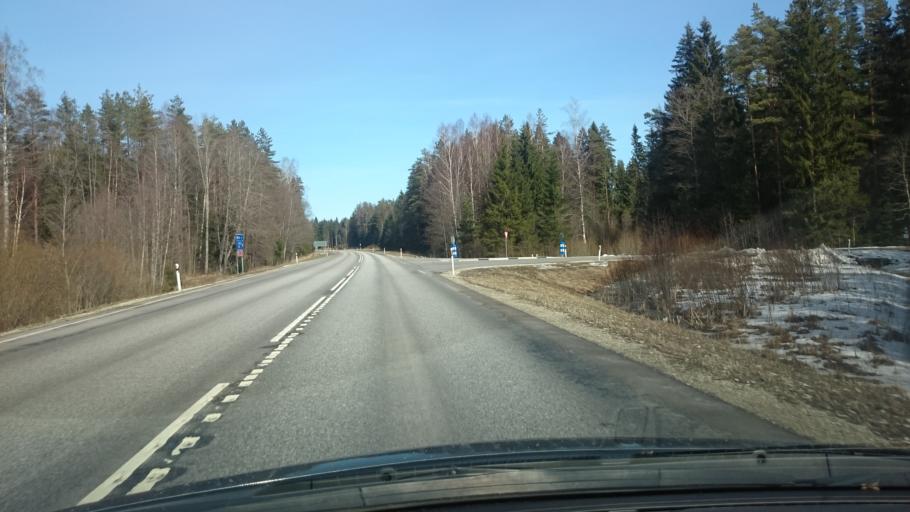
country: EE
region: Jaervamaa
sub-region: Tueri vald
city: Sarevere
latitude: 58.6968
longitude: 25.2556
